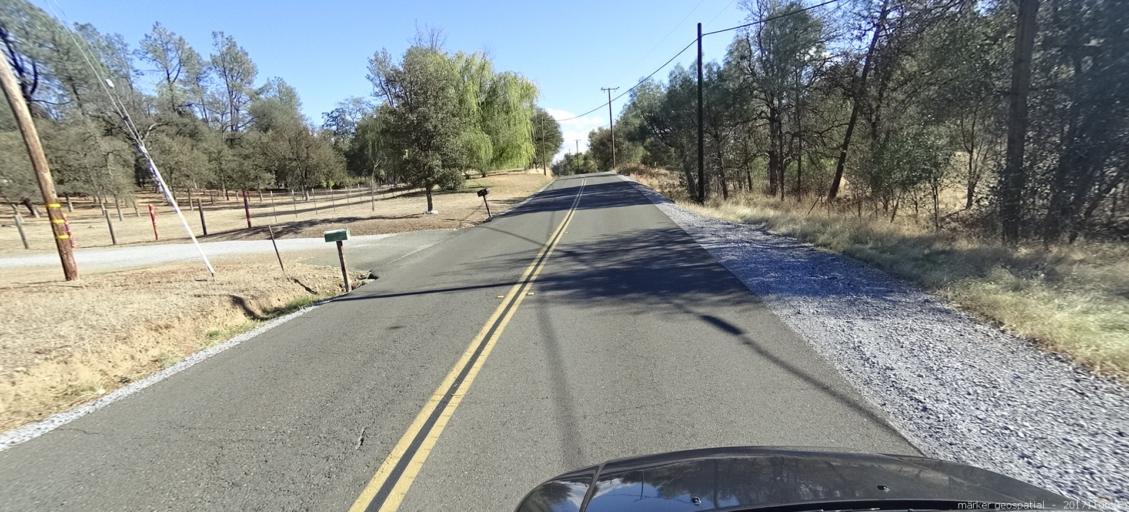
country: US
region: California
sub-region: Shasta County
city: Bella Vista
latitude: 40.6219
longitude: -122.2773
